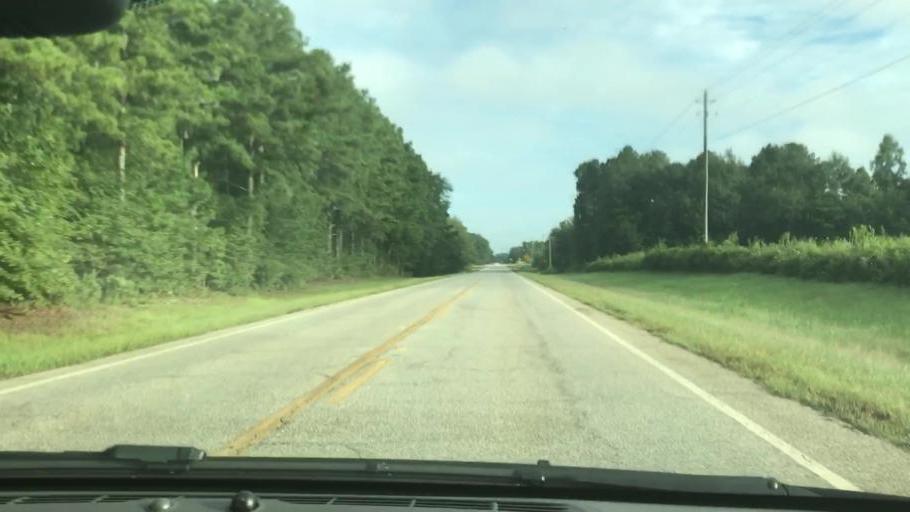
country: US
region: Georgia
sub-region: Clay County
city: Fort Gaines
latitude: 31.7268
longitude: -85.0455
